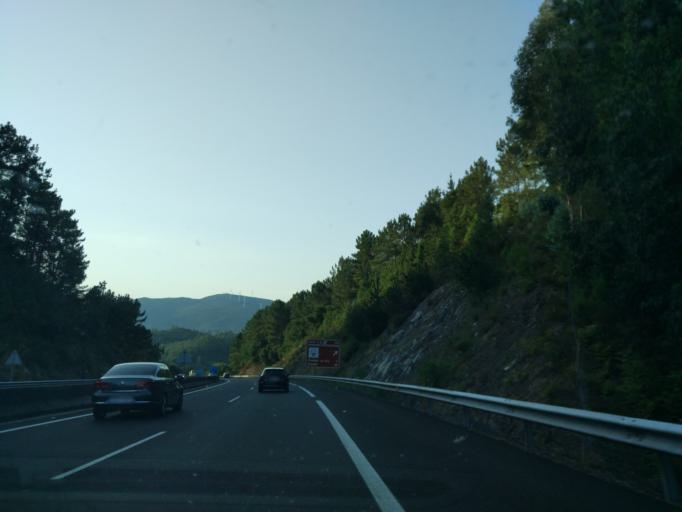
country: ES
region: Galicia
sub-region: Provincia de Pontevedra
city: Portas
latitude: 42.5782
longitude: -8.6732
